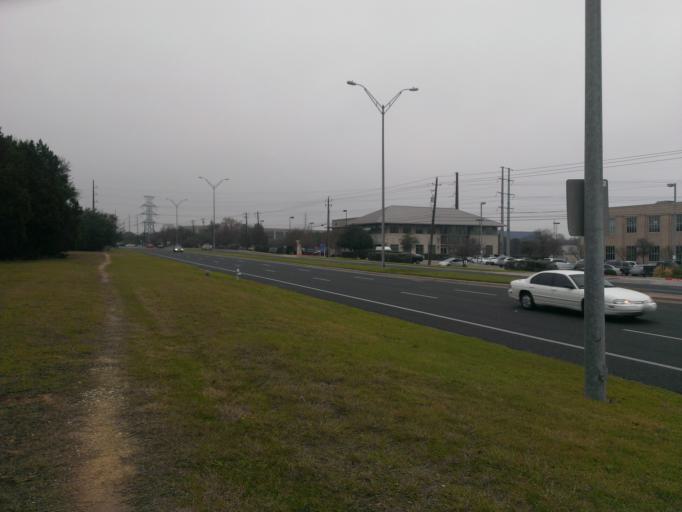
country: US
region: Texas
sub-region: Williamson County
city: Jollyville
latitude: 30.3990
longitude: -97.7399
